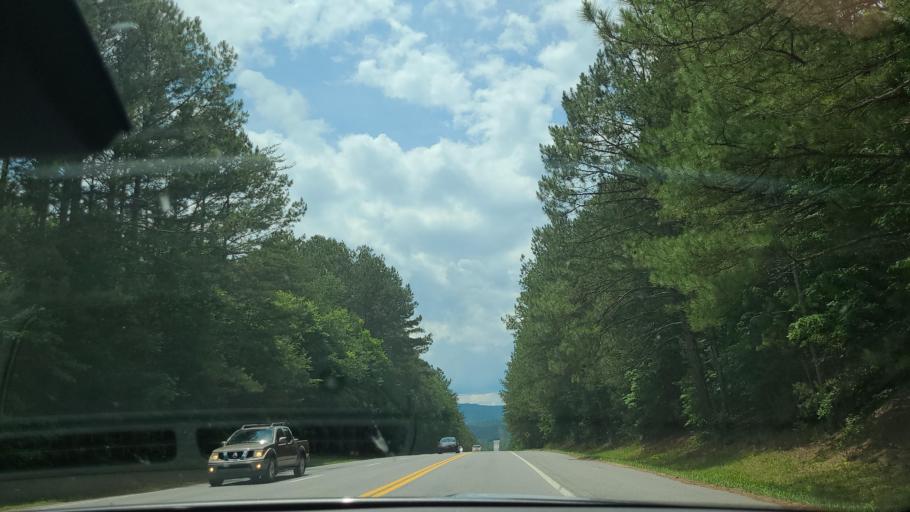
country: US
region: Georgia
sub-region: Fannin County
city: McCaysville
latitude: 35.0353
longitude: -84.4167
